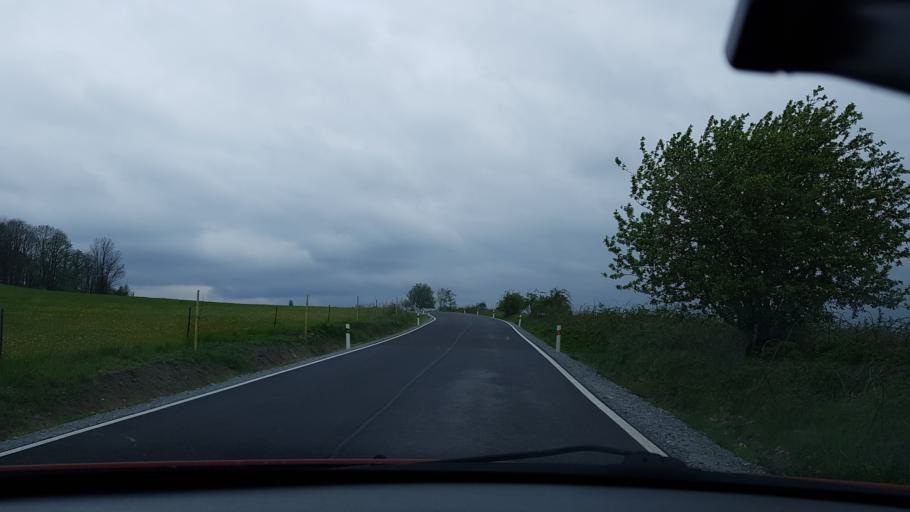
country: PL
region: Opole Voivodeship
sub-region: Powiat nyski
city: Kamienica
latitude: 50.4335
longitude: 16.9473
